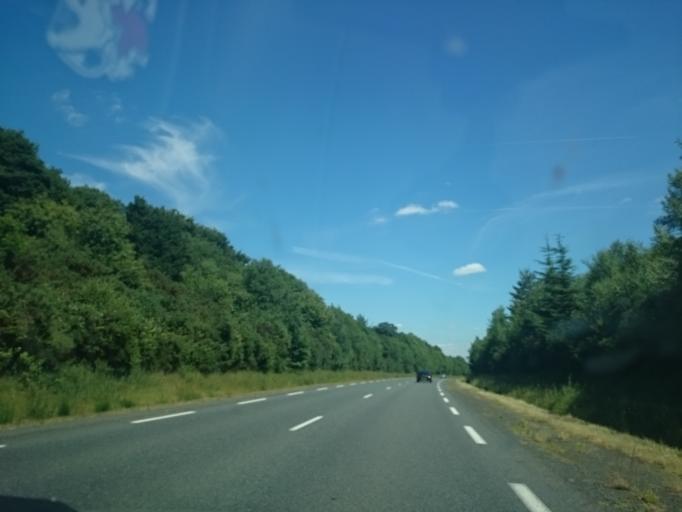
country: FR
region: Brittany
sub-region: Departement des Cotes-d'Armor
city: Plouguernevel
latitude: 48.2434
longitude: -3.2351
